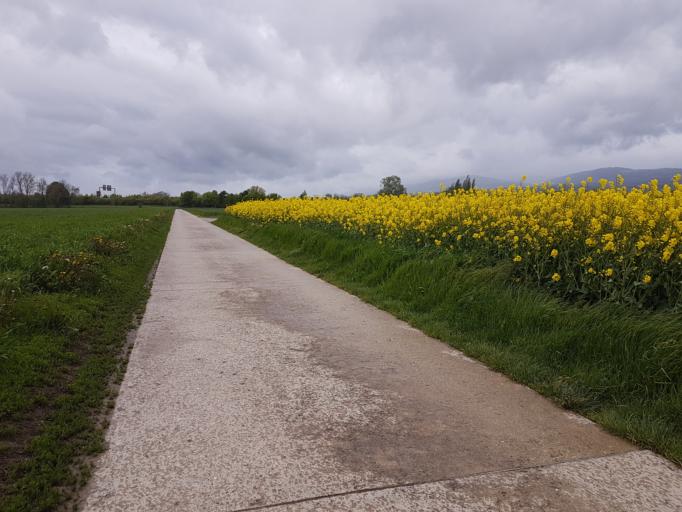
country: CH
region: Vaud
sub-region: Jura-Nord vaudois District
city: Chavornay
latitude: 46.7244
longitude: 6.5740
